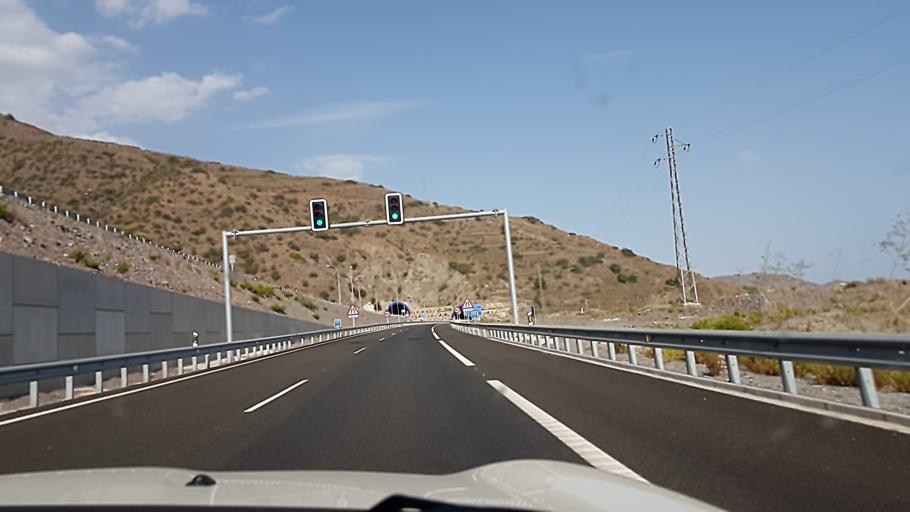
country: ES
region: Andalusia
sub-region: Provincia de Granada
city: Sorvilan
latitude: 36.7561
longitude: -3.2588
